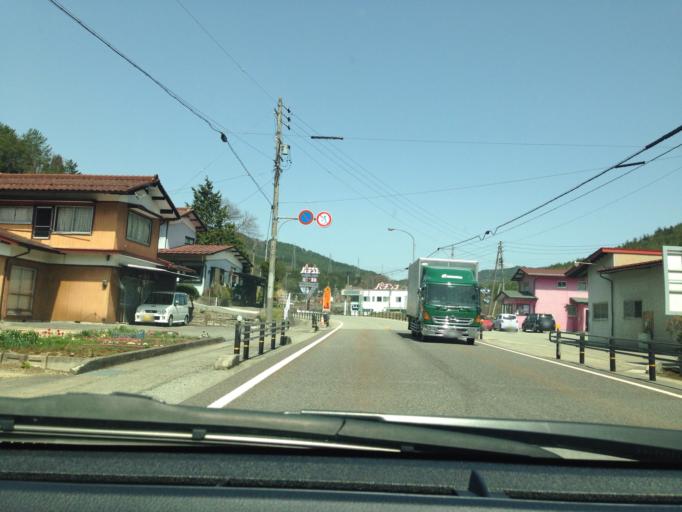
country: JP
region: Gifu
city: Takayama
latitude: 36.0613
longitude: 137.2704
